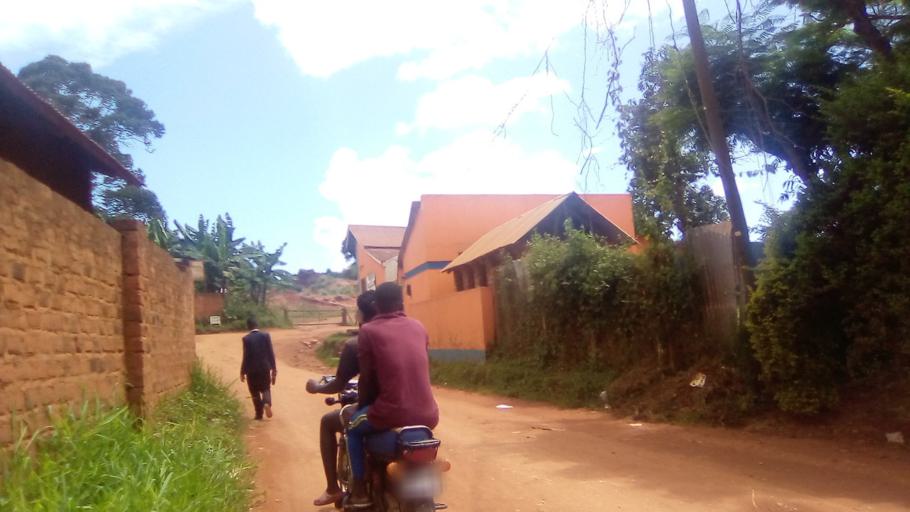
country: UG
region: Central Region
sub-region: Wakiso District
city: Entebbe
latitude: 0.1036
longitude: 32.5247
